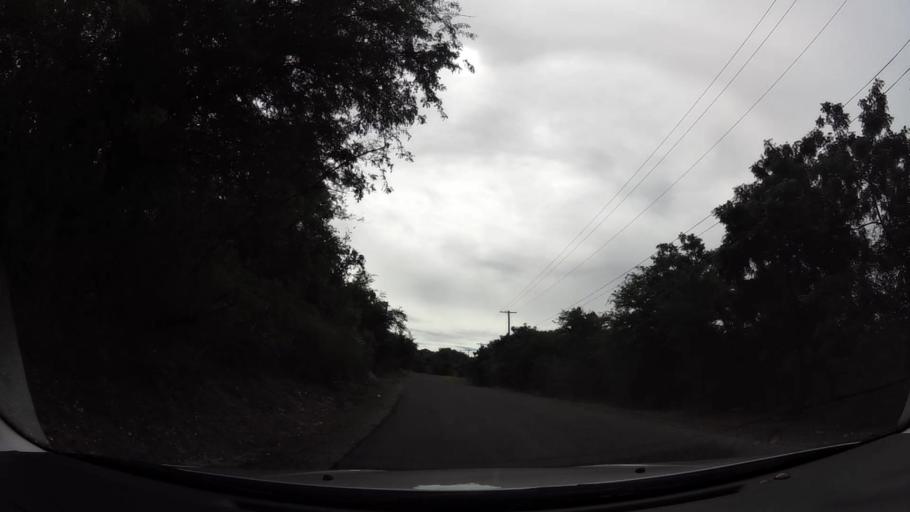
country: AG
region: Saint Peter
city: Parham
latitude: 17.0696
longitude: -61.7350
